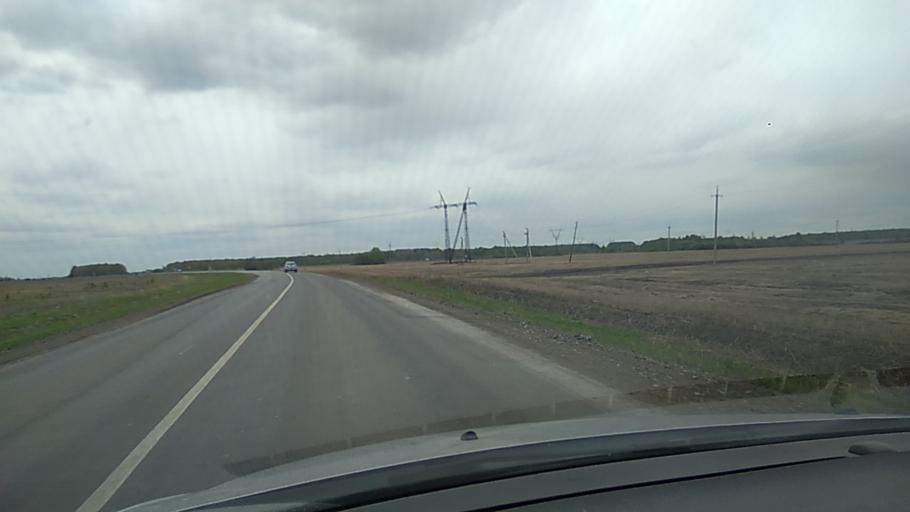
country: RU
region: Sverdlovsk
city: Martyush
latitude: 56.4109
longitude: 61.7973
